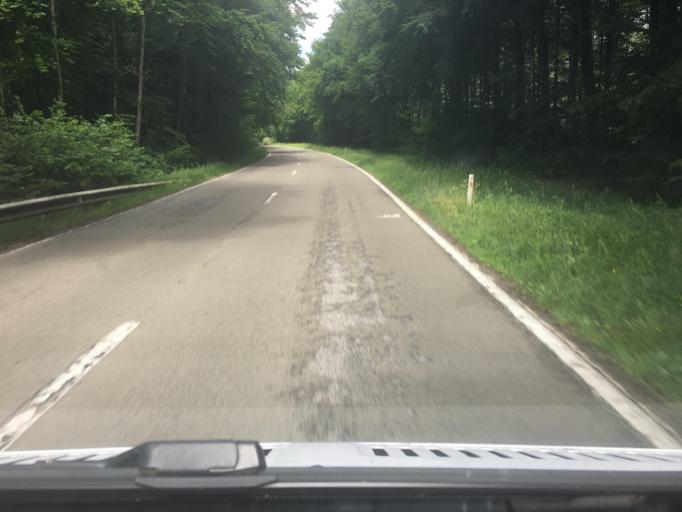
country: BE
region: Wallonia
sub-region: Province du Luxembourg
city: Florenville
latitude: 49.6454
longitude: 5.3415
